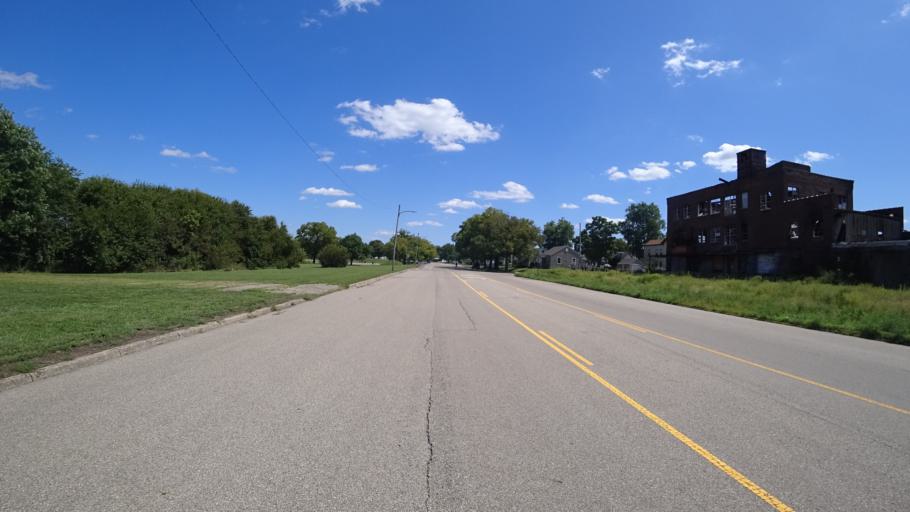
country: US
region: Ohio
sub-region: Butler County
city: Hamilton
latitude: 39.4057
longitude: -84.5531
